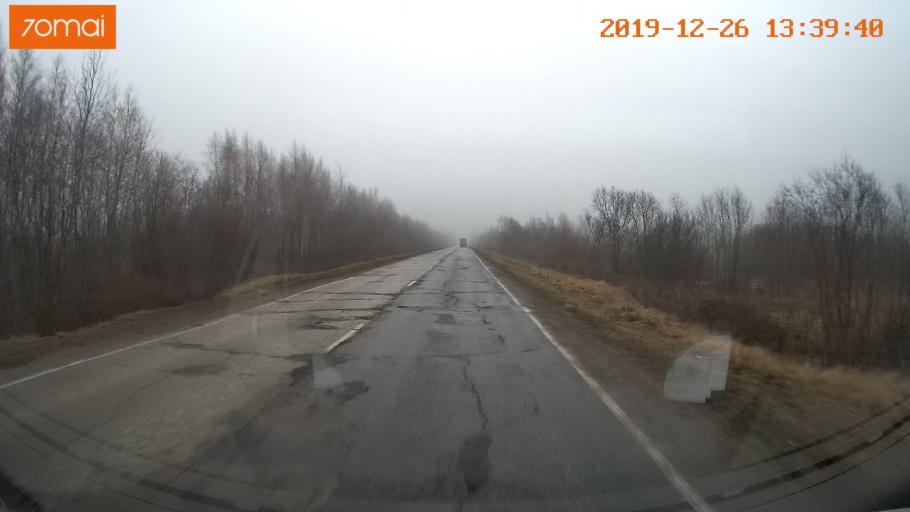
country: RU
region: Vologda
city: Sheksna
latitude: 58.7498
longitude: 38.4156
